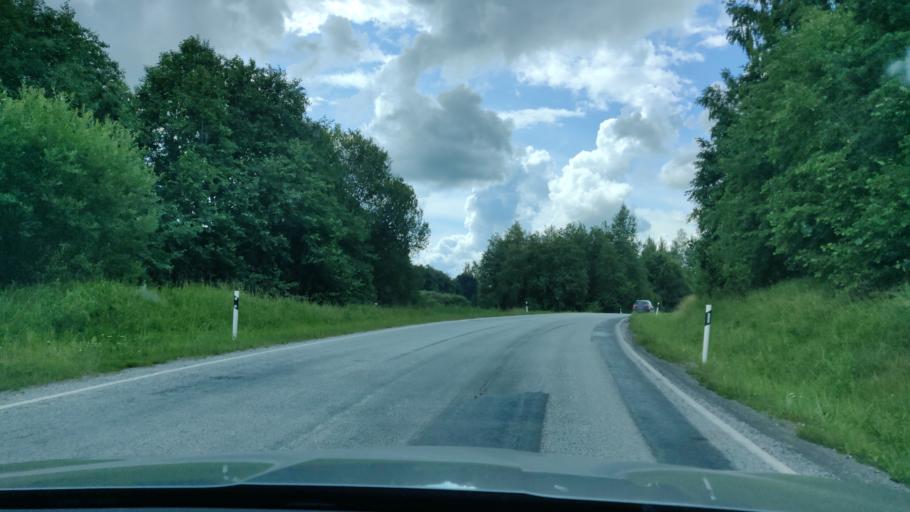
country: EE
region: Vorumaa
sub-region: Antsla vald
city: Vana-Antsla
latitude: 58.0266
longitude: 26.5092
